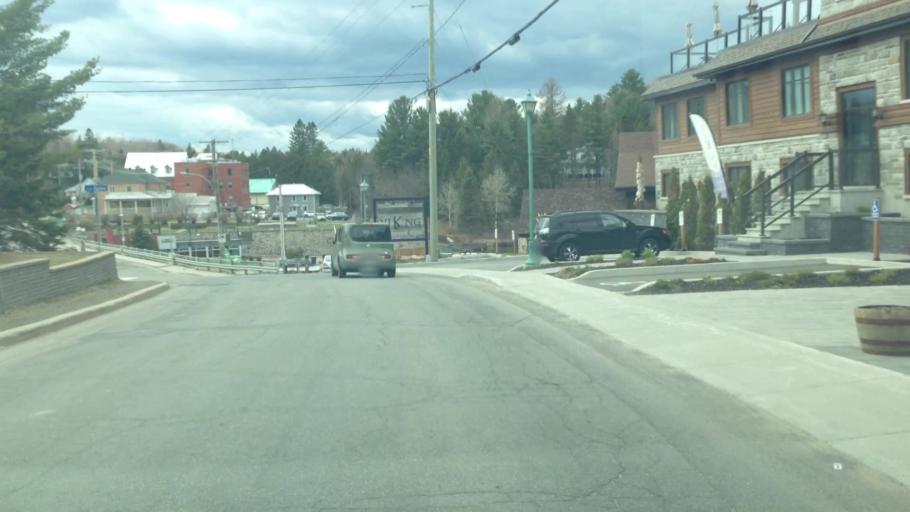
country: CA
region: Quebec
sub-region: Laurentides
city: Sainte-Adele
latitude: 46.0308
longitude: -74.0544
